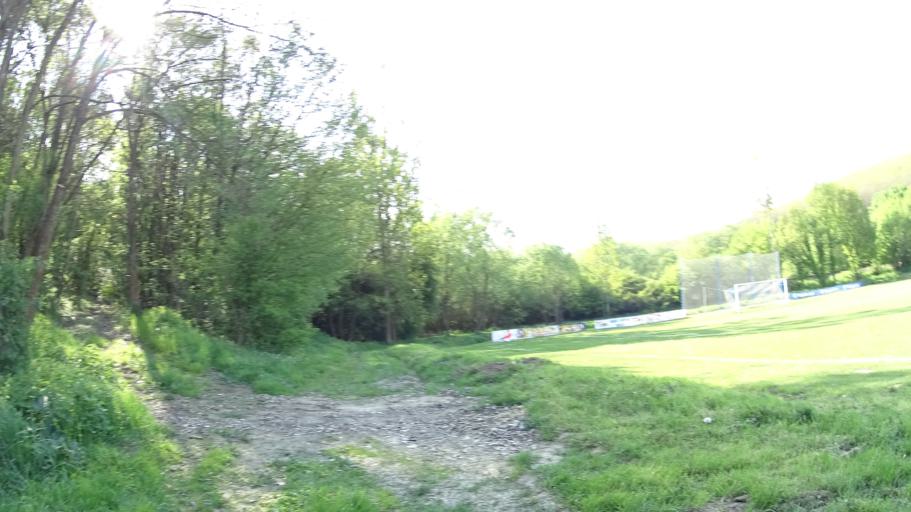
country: HU
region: Nograd
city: Retsag
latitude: 47.9152
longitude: 19.1799
